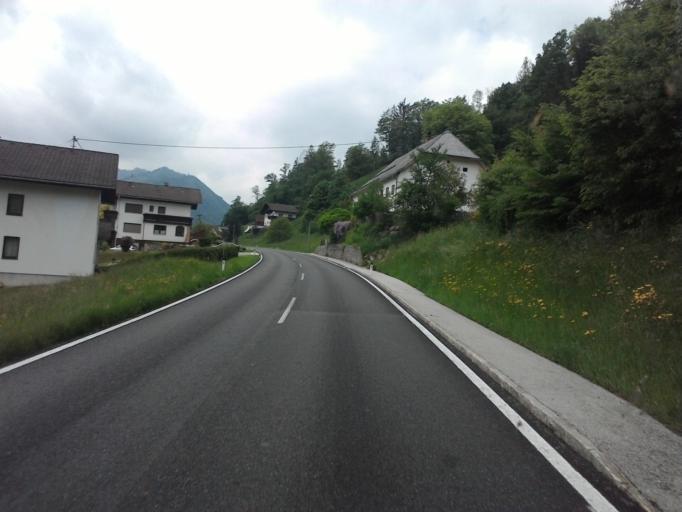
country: AT
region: Upper Austria
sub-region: Politischer Bezirk Steyr-Land
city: Maria Neustift
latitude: 47.8828
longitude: 14.5629
